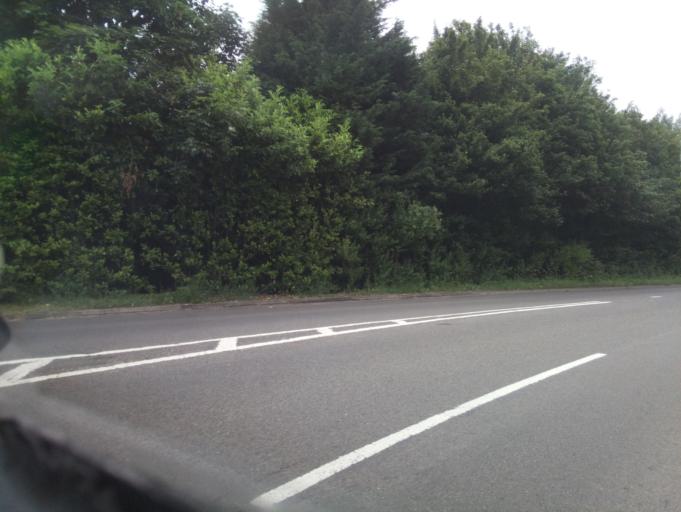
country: GB
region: England
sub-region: Staffordshire
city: Burton upon Trent
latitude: 52.8534
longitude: -1.6802
